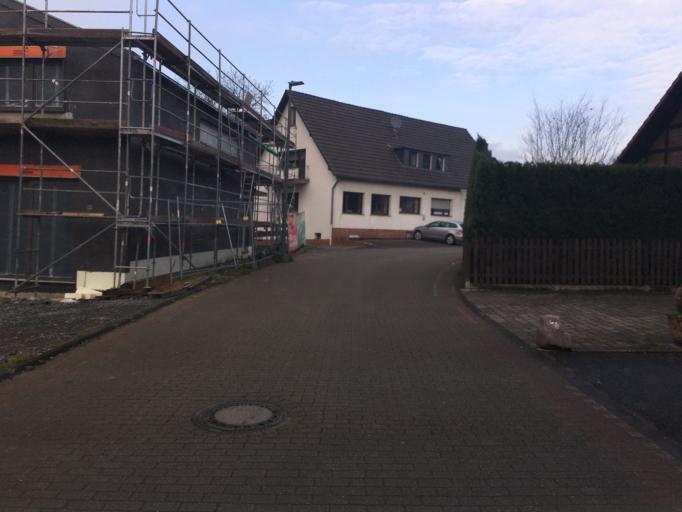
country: DE
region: North Rhine-Westphalia
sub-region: Regierungsbezirk Koln
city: Odenthal
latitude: 51.0182
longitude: 7.0977
